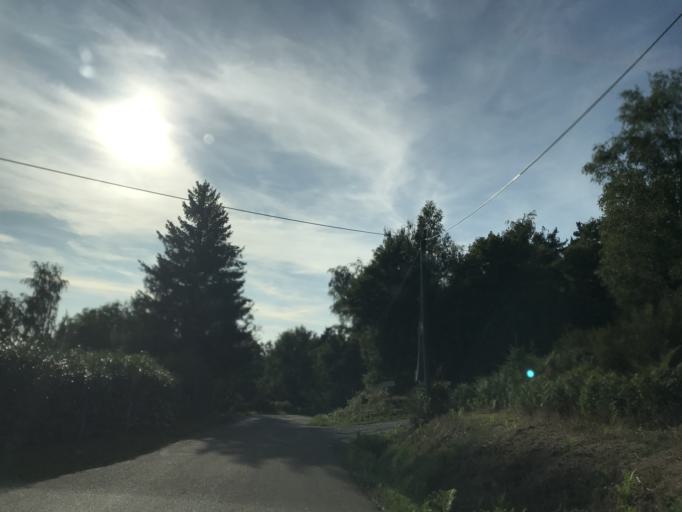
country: FR
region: Auvergne
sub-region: Departement du Puy-de-Dome
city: Job
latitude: 45.6765
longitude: 3.7326
